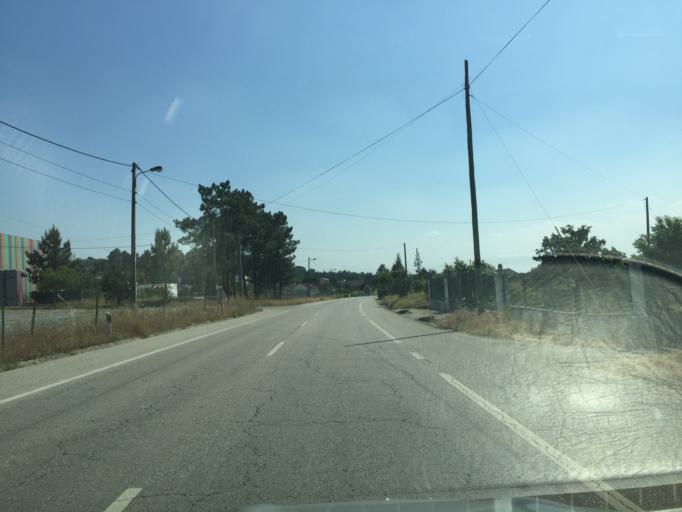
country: PT
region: Santarem
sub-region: Chamusca
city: Vila Nova da Barquinha
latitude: 39.4077
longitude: -8.4278
